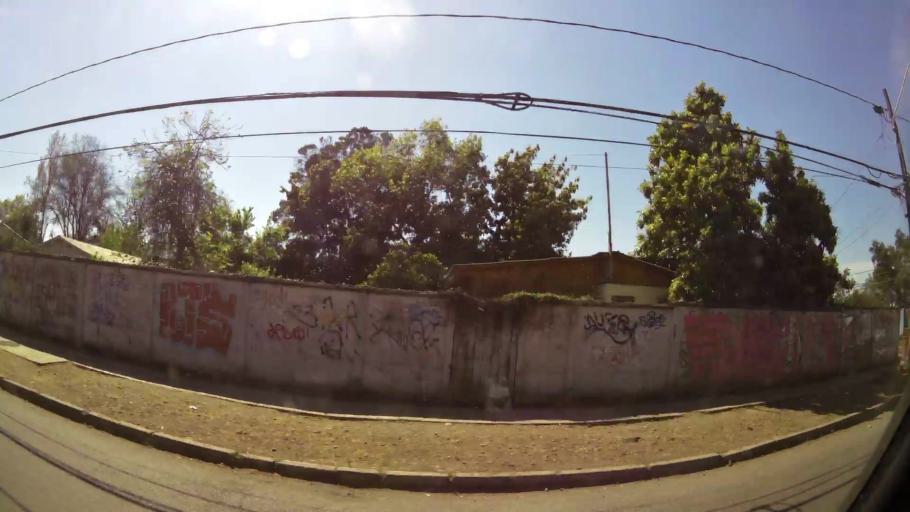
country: CL
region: Santiago Metropolitan
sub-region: Provincia de Talagante
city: Penaflor
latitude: -33.6091
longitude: -70.8838
